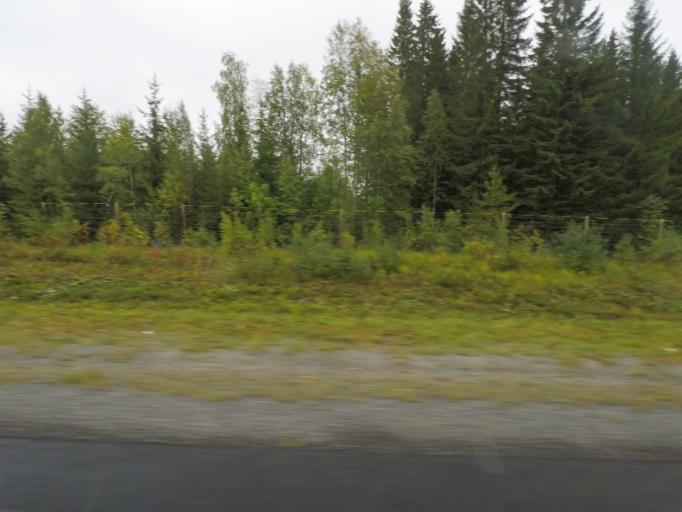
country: FI
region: Northern Savo
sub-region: Kuopio
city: Kuopio
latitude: 62.7700
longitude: 27.5844
